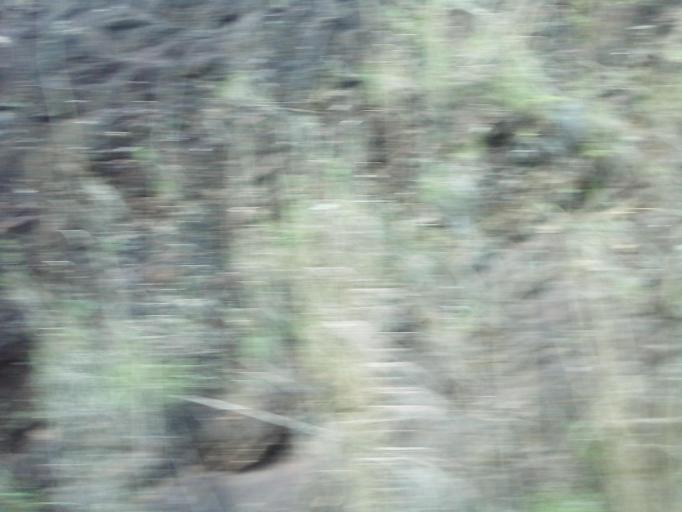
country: BR
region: Minas Gerais
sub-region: Caete
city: Caete
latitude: -19.9044
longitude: -43.7237
